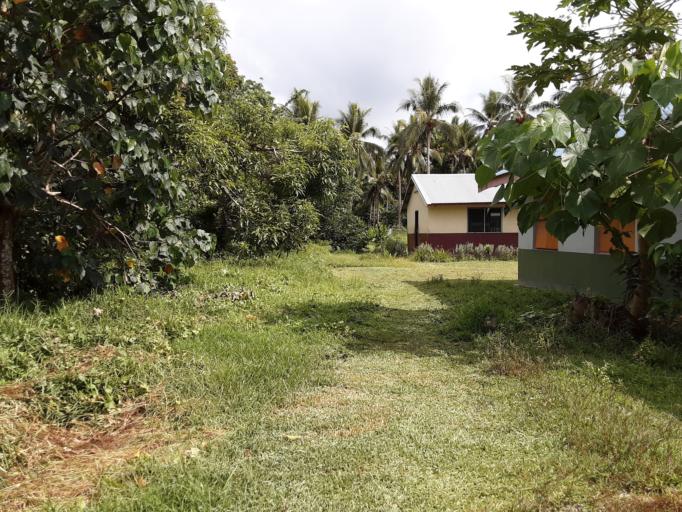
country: VU
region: Sanma
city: Luganville
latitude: -15.5805
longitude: 166.9995
